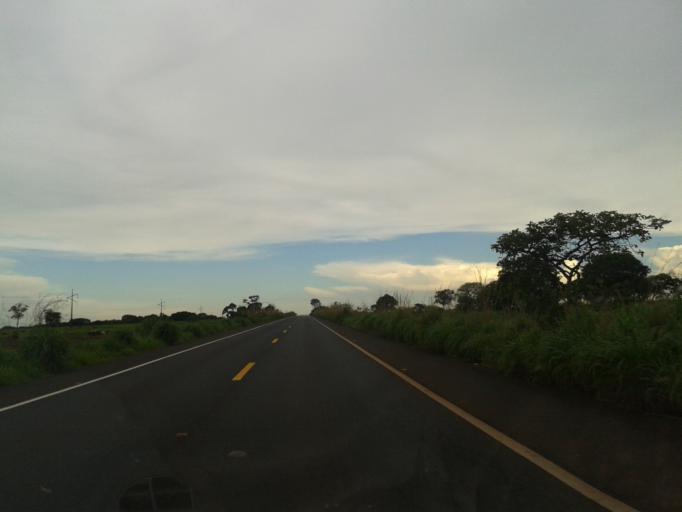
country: BR
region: Minas Gerais
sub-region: Santa Vitoria
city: Santa Vitoria
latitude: -18.9148
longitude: -50.2310
